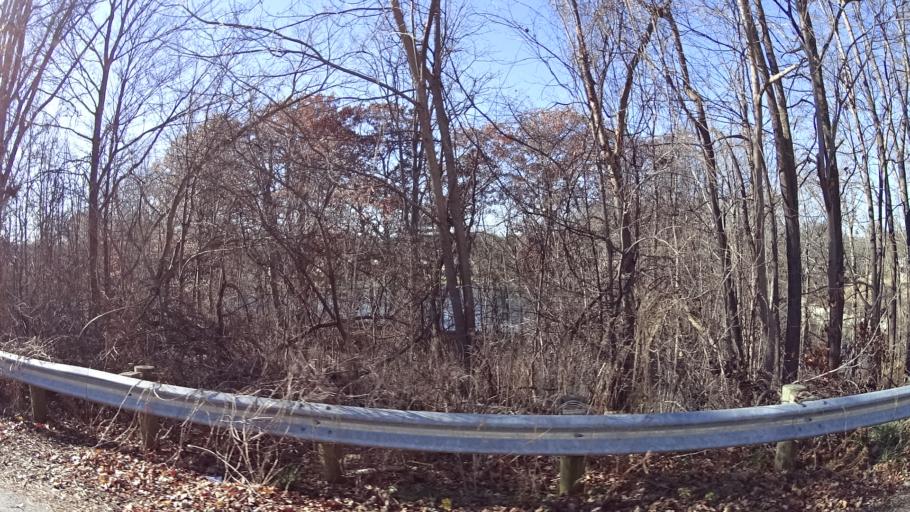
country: US
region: Ohio
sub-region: Lorain County
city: Elyria
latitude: 41.3322
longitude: -82.0692
